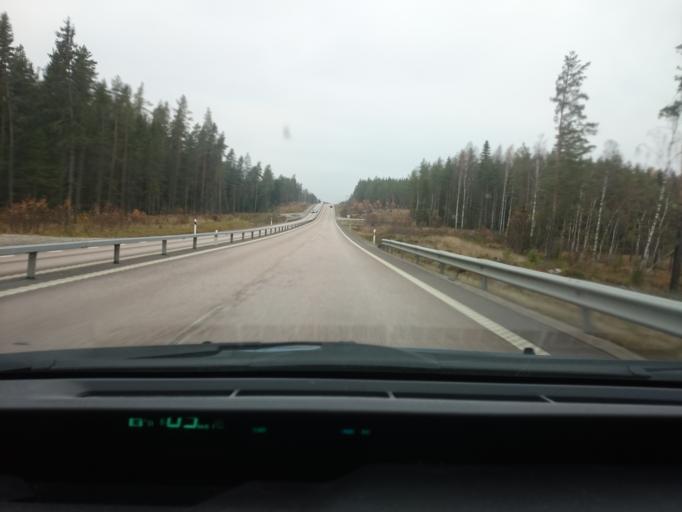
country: SE
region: Vaestmanland
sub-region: Sala Kommun
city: Sala
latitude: 60.0079
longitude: 16.4003
